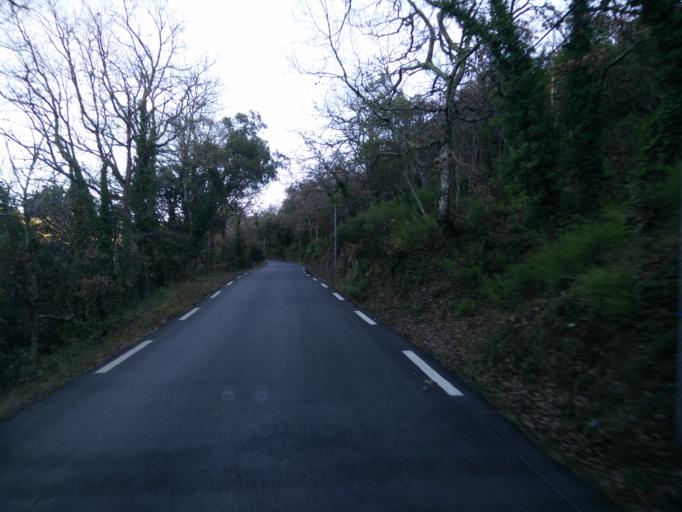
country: FR
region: Provence-Alpes-Cote d'Azur
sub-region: Departement du Var
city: Collobrieres
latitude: 43.2285
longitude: 6.2886
